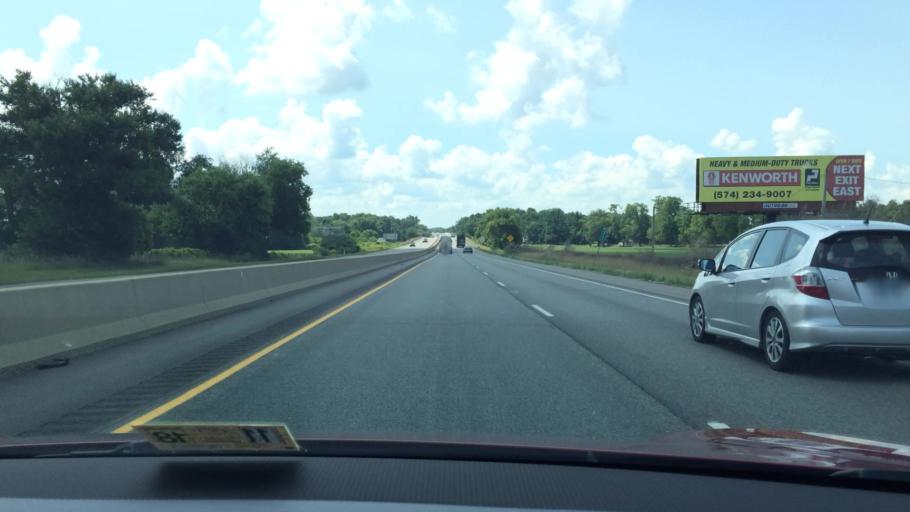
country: US
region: Indiana
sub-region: Saint Joseph County
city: South Bend
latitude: 41.6985
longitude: -86.3404
